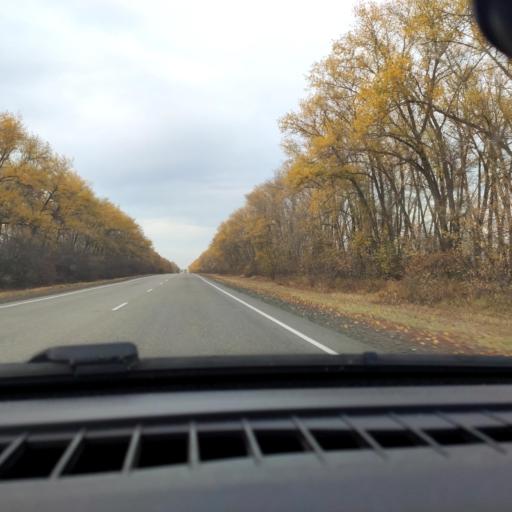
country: RU
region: Voronezj
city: Ostrogozhsk
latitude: 50.9895
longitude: 38.9975
